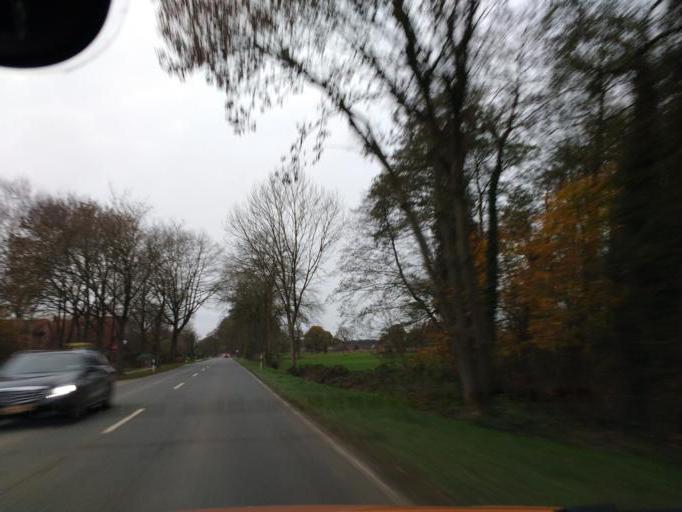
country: DE
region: Lower Saxony
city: Hude
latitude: 53.0655
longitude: 8.4352
